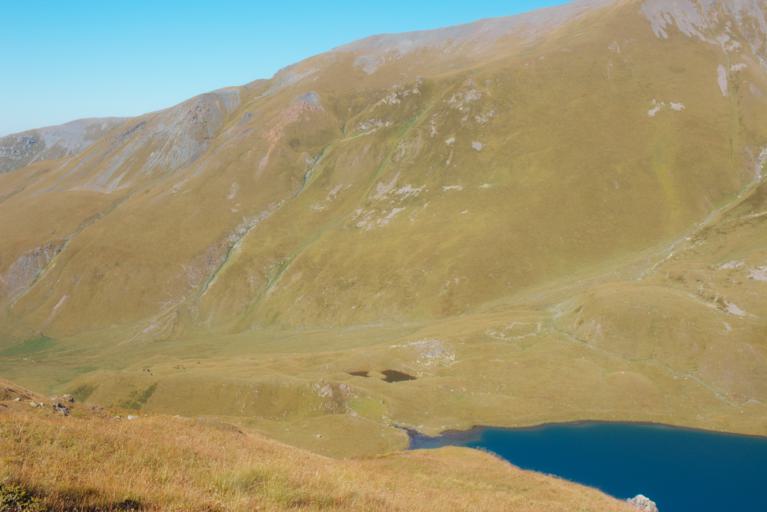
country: RU
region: Karachayevo-Cherkesiya
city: Mednogorskiy
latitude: 43.6164
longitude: 41.1443
